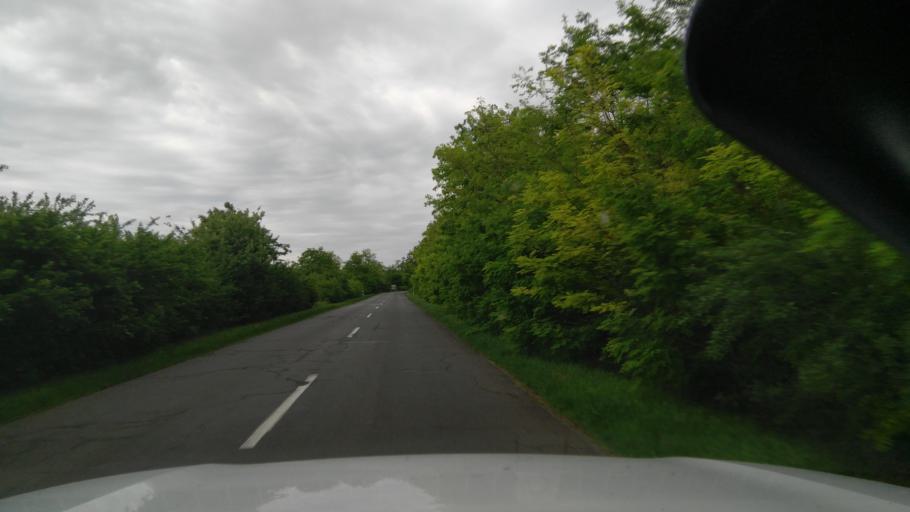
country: HU
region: Bekes
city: Bekescsaba
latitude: 46.6797
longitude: 21.1679
